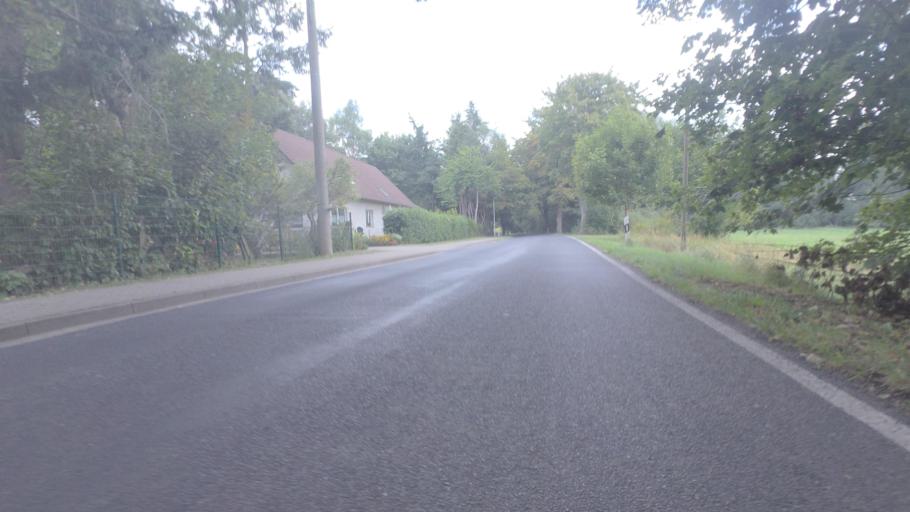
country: DE
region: Mecklenburg-Vorpommern
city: Borrentin
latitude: 53.8516
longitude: 12.9658
